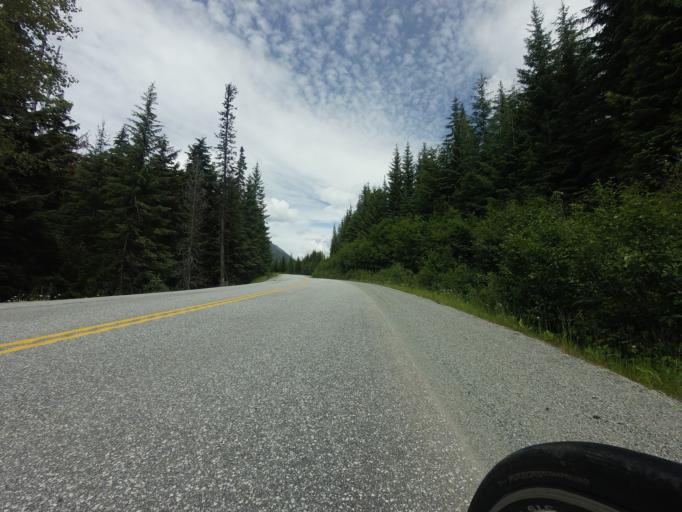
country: CA
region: British Columbia
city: Pemberton
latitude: 50.3891
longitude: -122.3455
